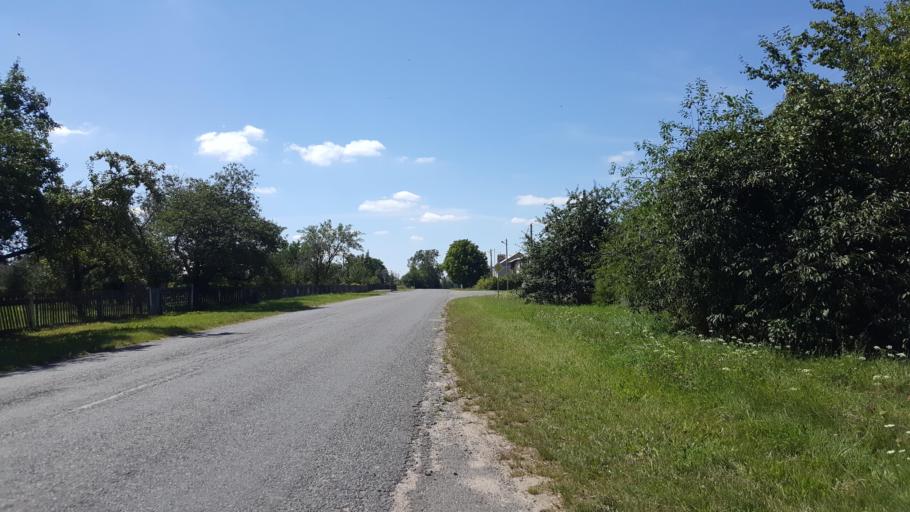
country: BY
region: Brest
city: Kamyanyets
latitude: 52.3686
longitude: 23.6270
